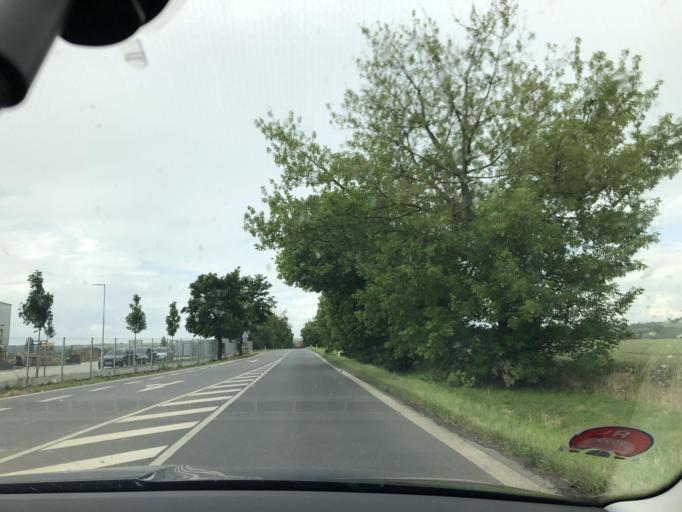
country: CZ
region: Central Bohemia
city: Horomerice
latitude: 50.1425
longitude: 14.3424
